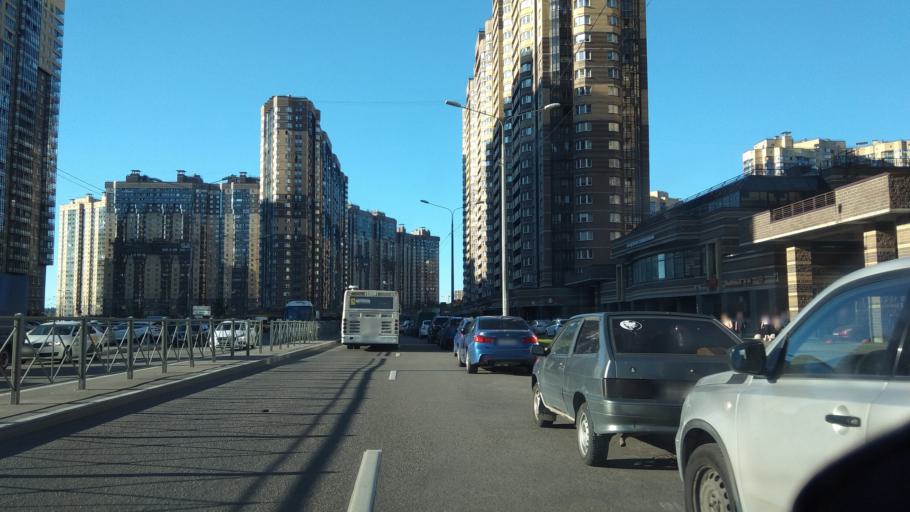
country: RU
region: Leningrad
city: Parnas
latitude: 60.0771
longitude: 30.3429
